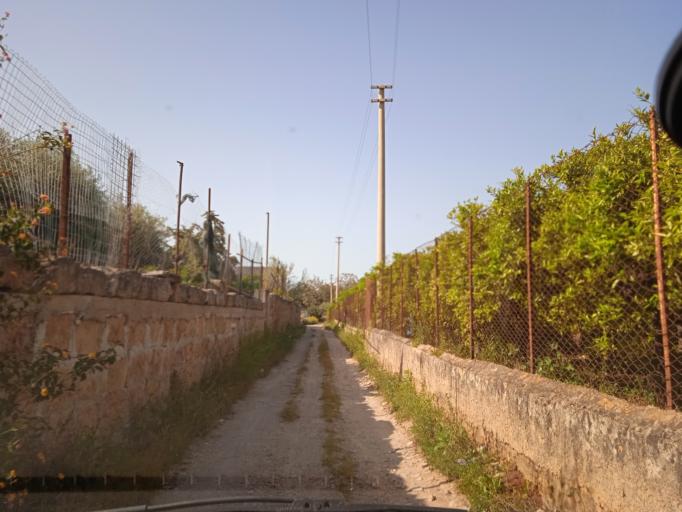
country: IT
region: Sicily
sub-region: Palermo
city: Villabate
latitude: 38.0807
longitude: 13.4515
